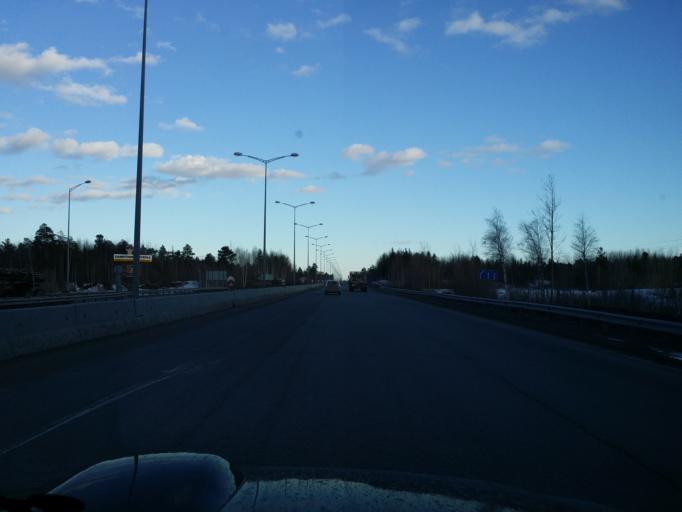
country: RU
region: Khanty-Mansiyskiy Avtonomnyy Okrug
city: Nizhnevartovsk
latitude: 61.0067
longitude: 76.4084
